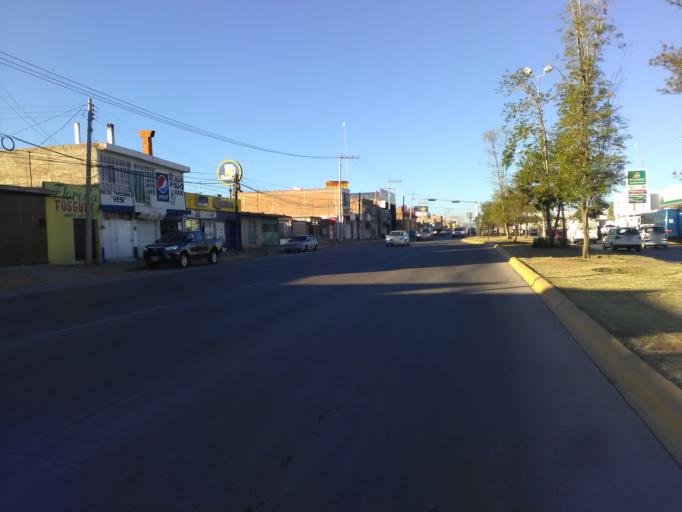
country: MX
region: Durango
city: Victoria de Durango
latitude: 24.0490
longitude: -104.6492
